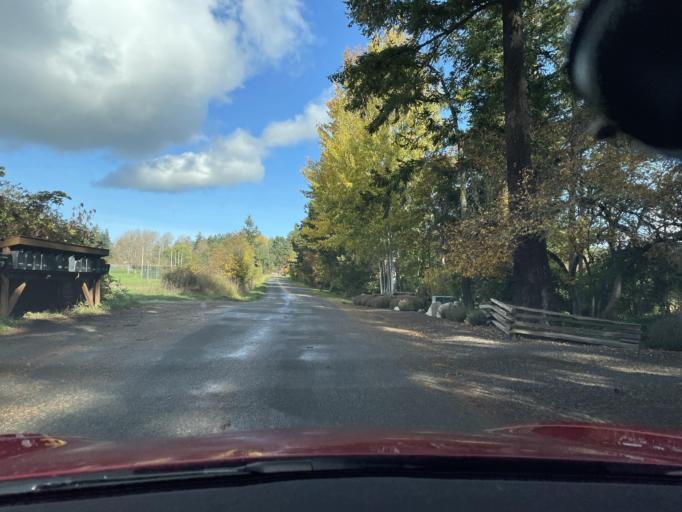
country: US
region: Washington
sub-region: San Juan County
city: Friday Harbor
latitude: 48.5012
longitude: -123.0230
